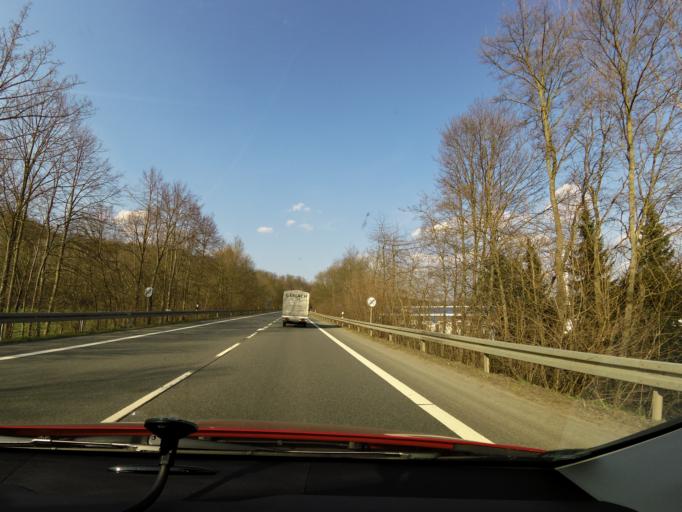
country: DE
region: Lower Saxony
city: Herzberg am Harz
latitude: 51.6466
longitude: 10.3175
